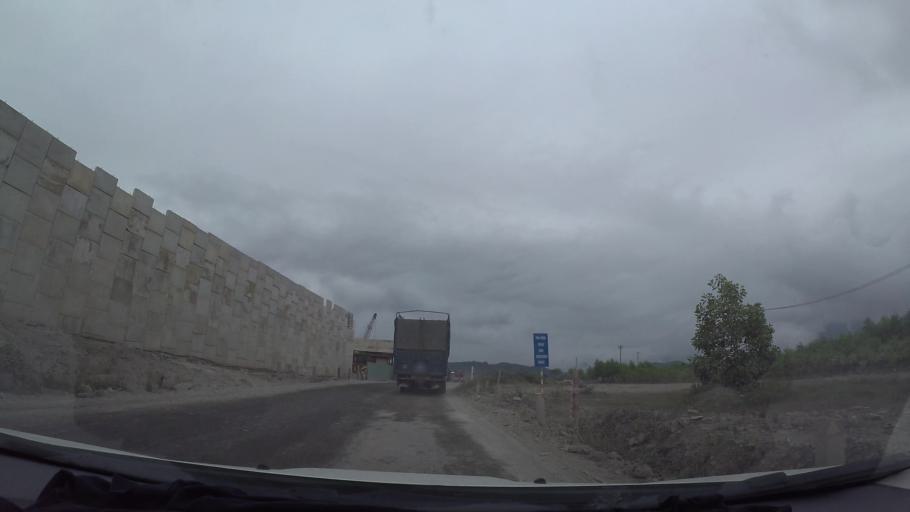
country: VN
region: Da Nang
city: Lien Chieu
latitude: 16.0948
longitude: 108.0879
